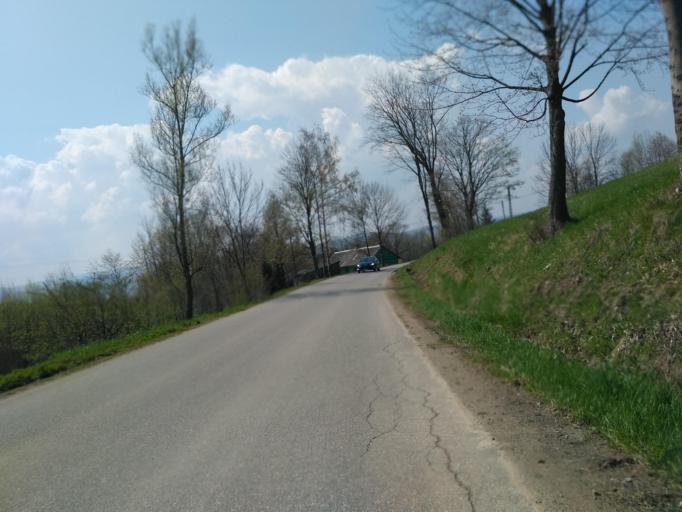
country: PL
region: Subcarpathian Voivodeship
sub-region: Powiat sanocki
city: Zarszyn
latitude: 49.5510
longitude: 21.9877
